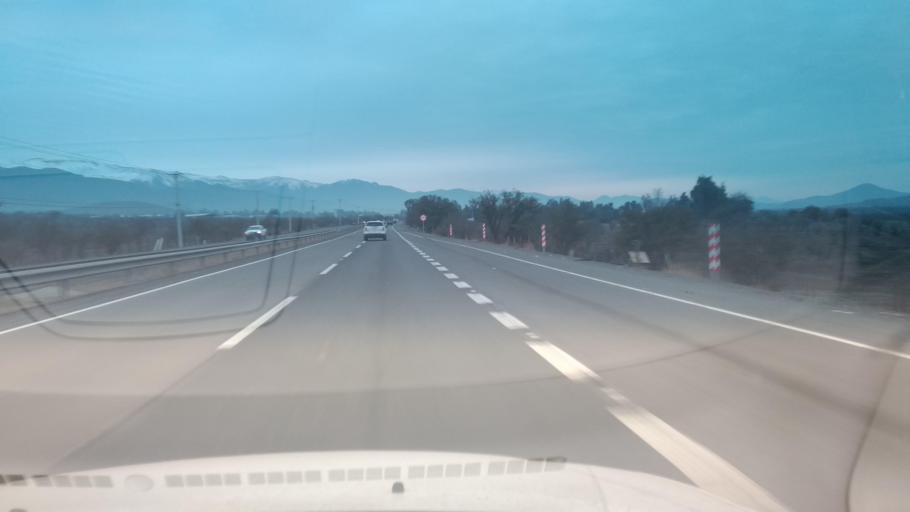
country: CL
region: Santiago Metropolitan
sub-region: Provincia de Chacabuco
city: Chicureo Abajo
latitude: -33.1248
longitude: -70.6751
